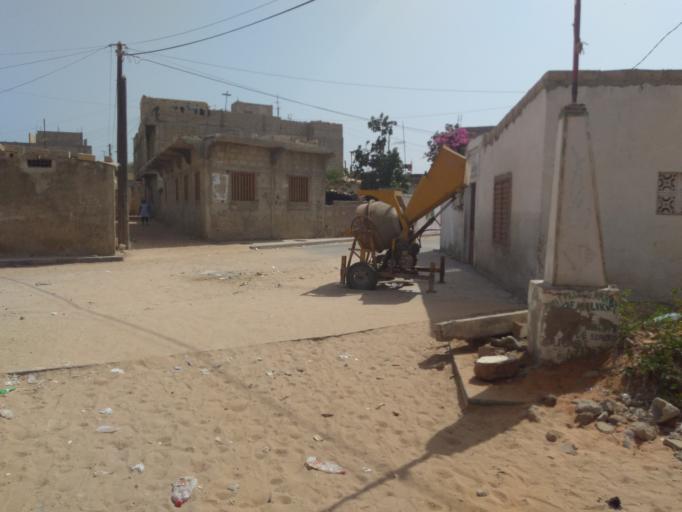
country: SN
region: Dakar
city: Pikine
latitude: 14.7939
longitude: -17.3381
